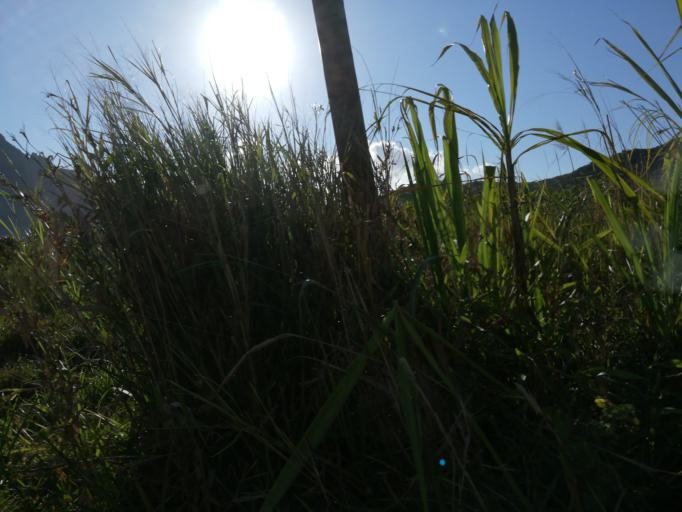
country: MU
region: Moka
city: Saint Pierre
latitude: -20.2086
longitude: 57.5264
